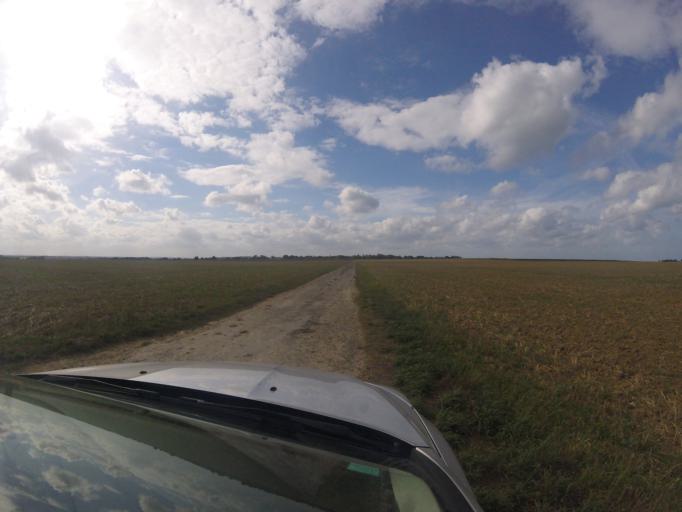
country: FR
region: Lower Normandy
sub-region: Departement du Calvados
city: Saint-Vigor-le-Grand
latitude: 49.3359
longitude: -0.6754
